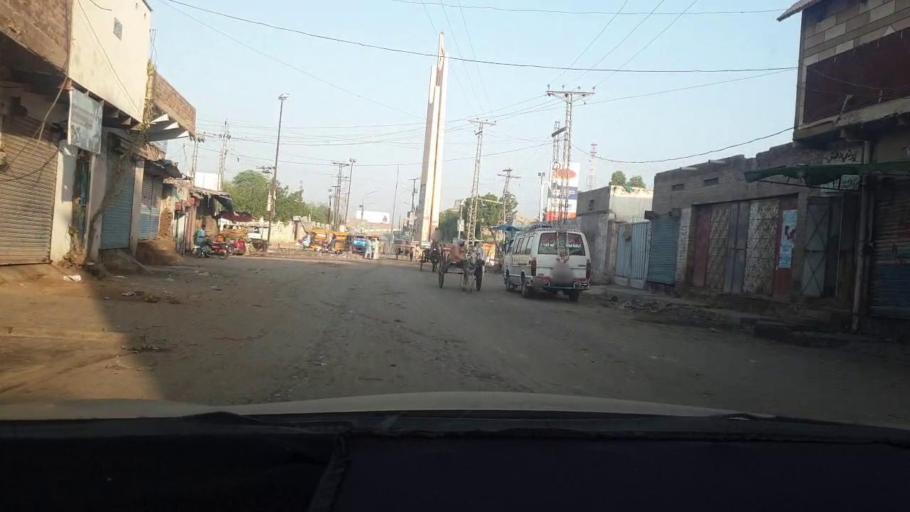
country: PK
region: Sindh
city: Larkana
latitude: 27.5428
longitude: 68.2128
